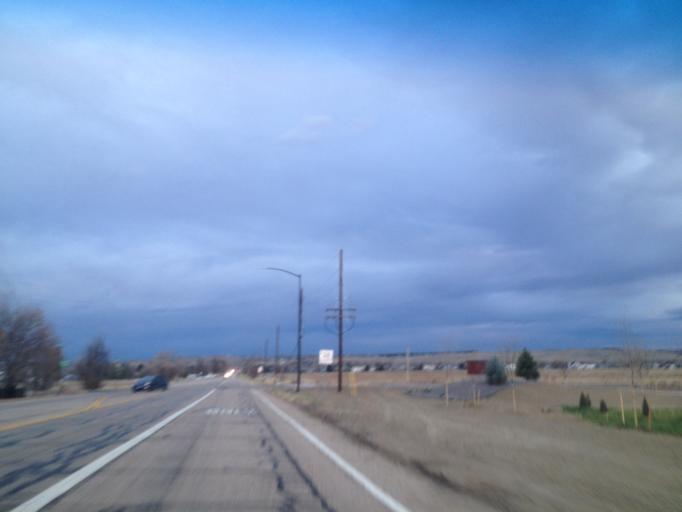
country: US
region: Colorado
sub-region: Boulder County
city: Louisville
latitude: 39.9724
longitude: -105.1103
